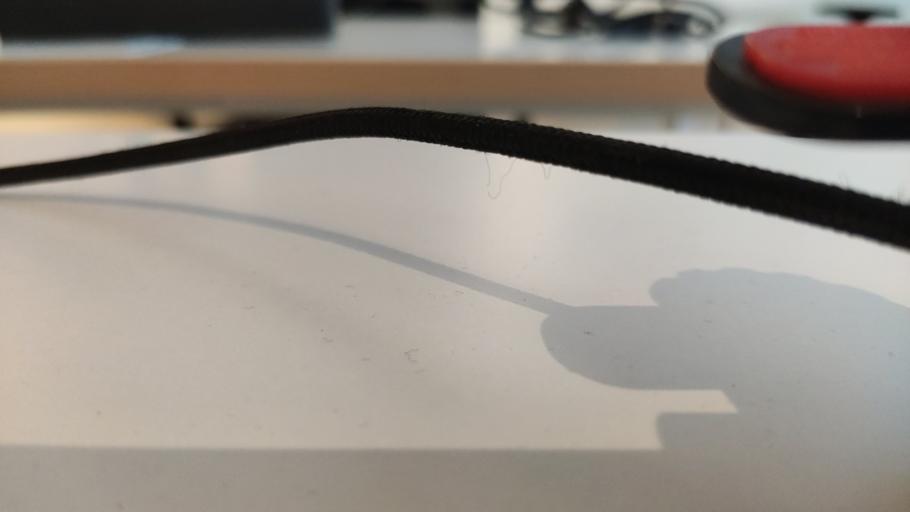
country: RU
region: Moskovskaya
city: Novopetrovskoye
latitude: 55.9150
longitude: 36.4402
